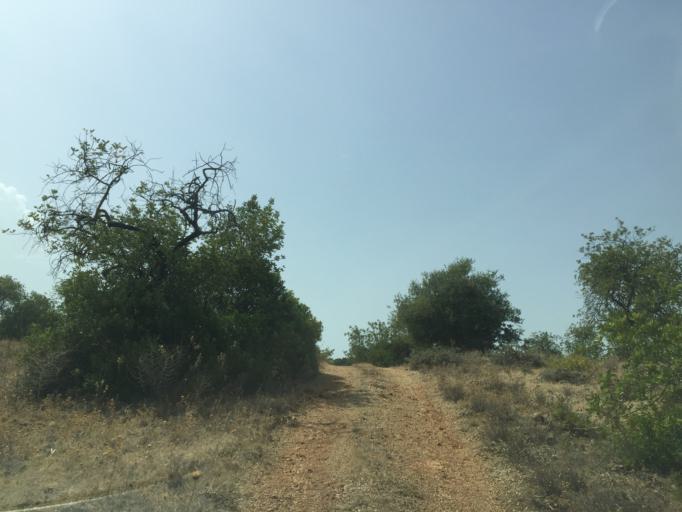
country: PT
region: Faro
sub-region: Loule
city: Boliqueime
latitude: 37.1342
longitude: -8.1383
